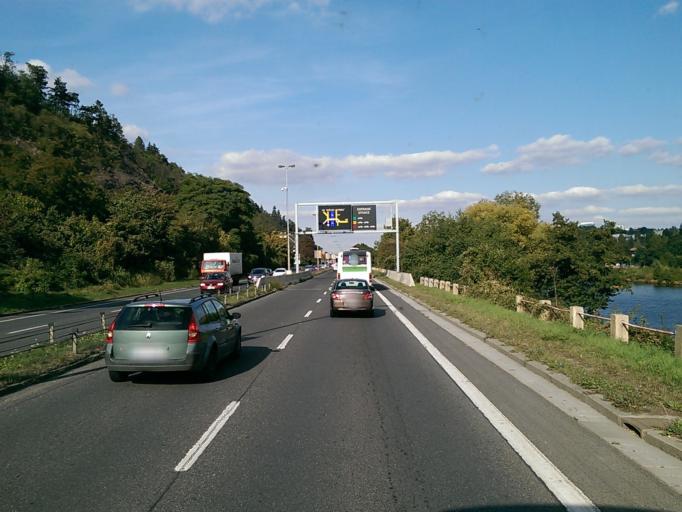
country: CZ
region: Praha
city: Branik
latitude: 50.0285
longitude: 14.3971
